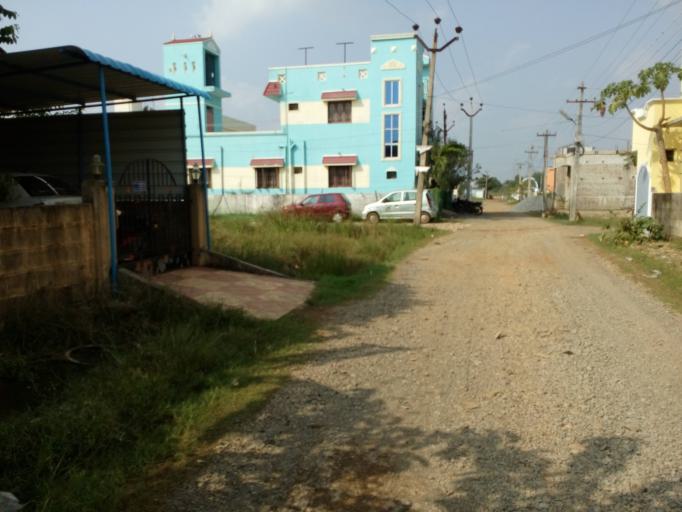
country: IN
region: Tamil Nadu
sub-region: Thiruvallur
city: Vellanur
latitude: 13.1509
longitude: 80.1107
